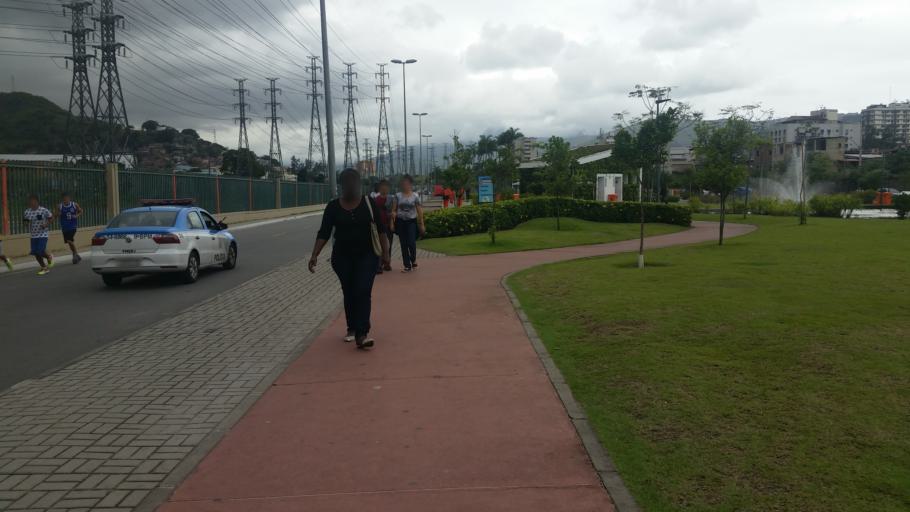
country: BR
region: Rio de Janeiro
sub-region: Sao Joao De Meriti
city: Sao Joao de Meriti
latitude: -22.8651
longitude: -43.3438
